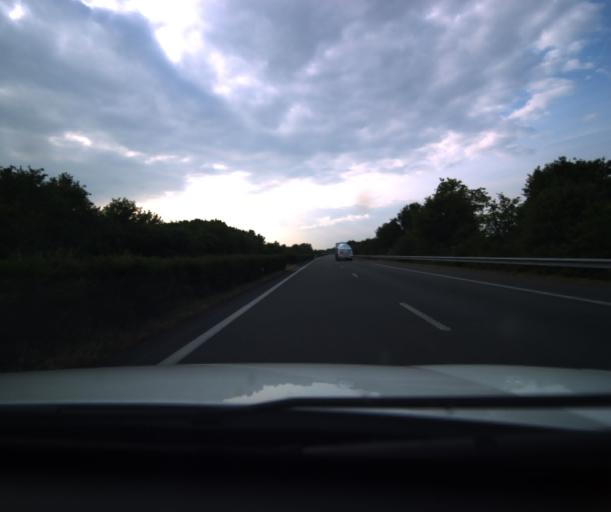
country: FR
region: Midi-Pyrenees
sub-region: Departement du Tarn-et-Garonne
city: Montech
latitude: 43.9948
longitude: 1.2309
